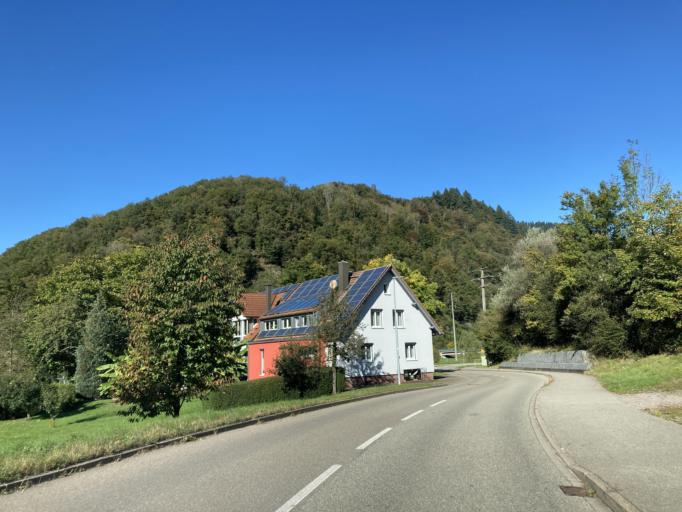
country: DE
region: Baden-Wuerttemberg
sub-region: Freiburg Region
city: Wolfach
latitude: 48.2818
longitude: 8.2143
